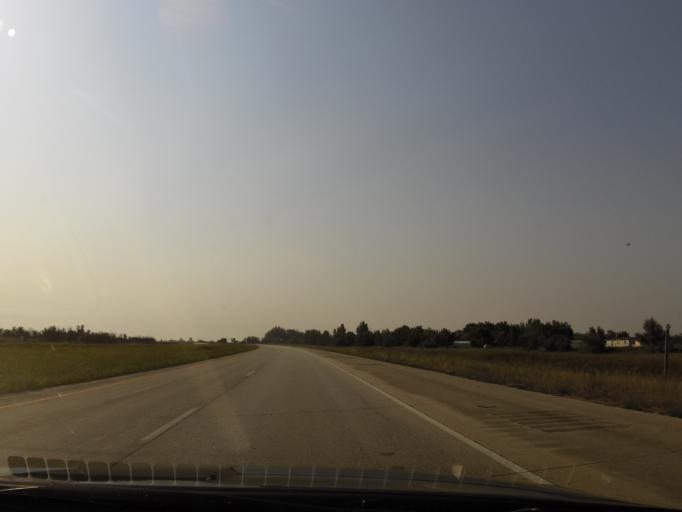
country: US
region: North Dakota
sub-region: Grand Forks County
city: Grand Forks
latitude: 48.0707
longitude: -97.1687
